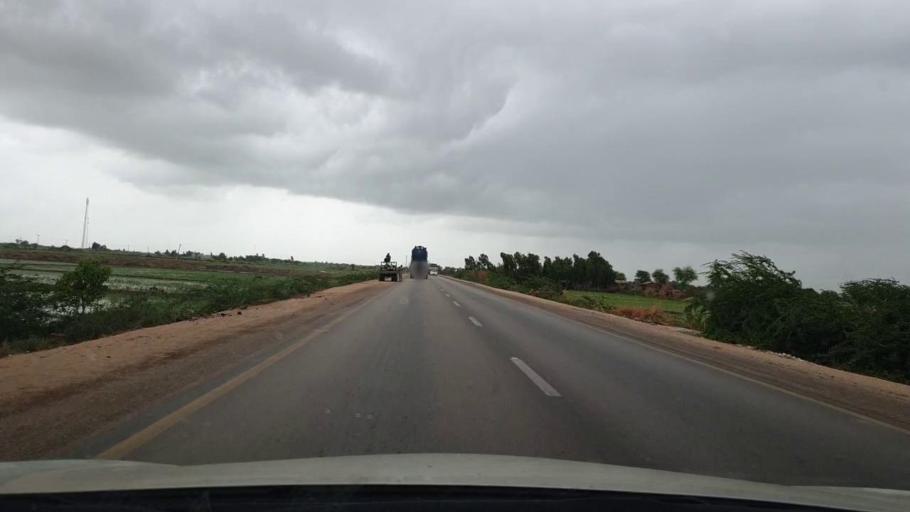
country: PK
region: Sindh
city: Kario
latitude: 24.6444
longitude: 68.4790
